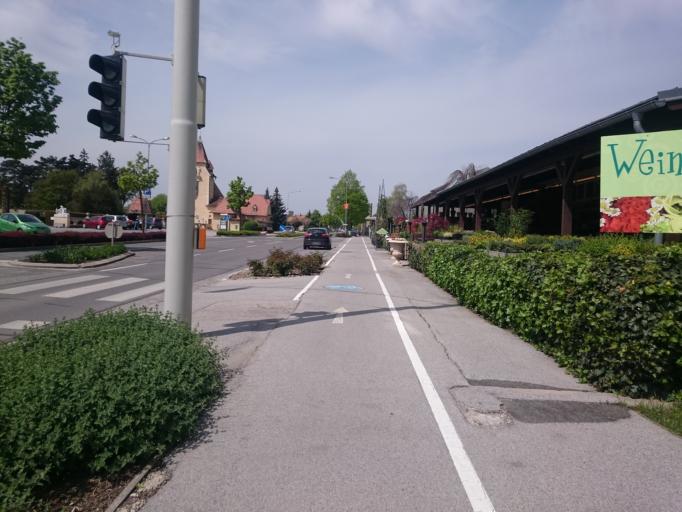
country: AT
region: Lower Austria
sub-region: Politischer Bezirk Korneuburg
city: Korneuburg
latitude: 48.3501
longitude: 16.3256
